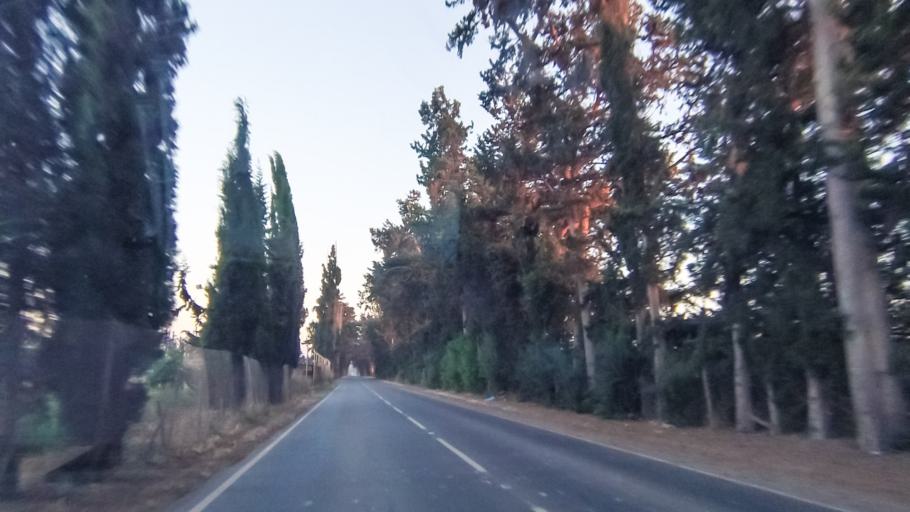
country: CY
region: Larnaka
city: Kolossi
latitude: 34.6418
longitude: 32.9450
